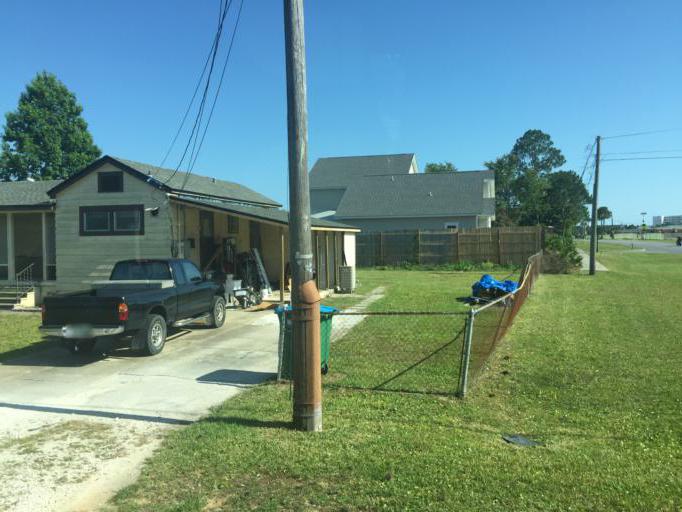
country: US
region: Florida
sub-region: Bay County
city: Panama City Beach
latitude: 30.2022
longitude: -85.8359
